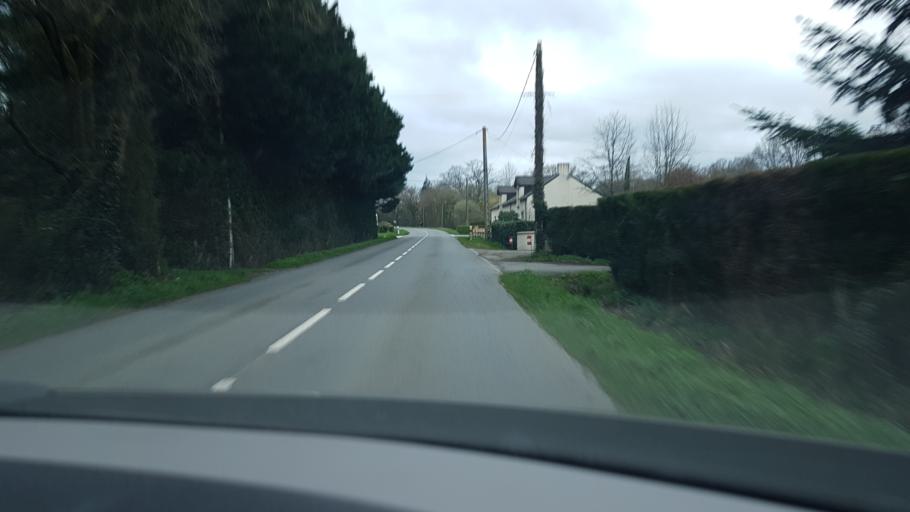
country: FR
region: Pays de la Loire
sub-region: Departement de la Loire-Atlantique
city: La Grigonnais
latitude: 47.5171
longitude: -1.6525
